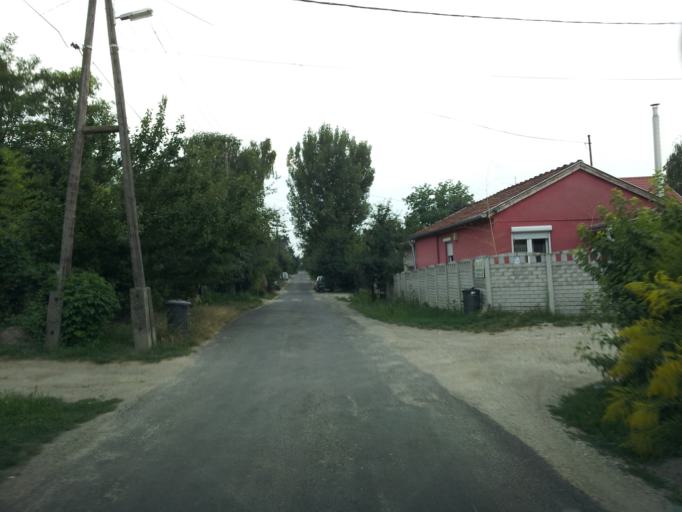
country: HU
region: Pest
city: Szigetszentmiklos
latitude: 47.3098
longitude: 19.0358
